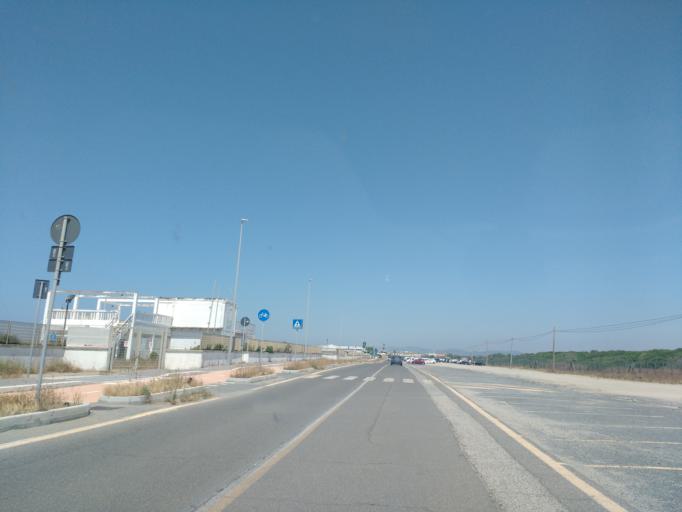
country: IT
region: Latium
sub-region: Citta metropolitana di Roma Capitale
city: Passo Oscuro
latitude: 41.8834
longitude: 12.1722
